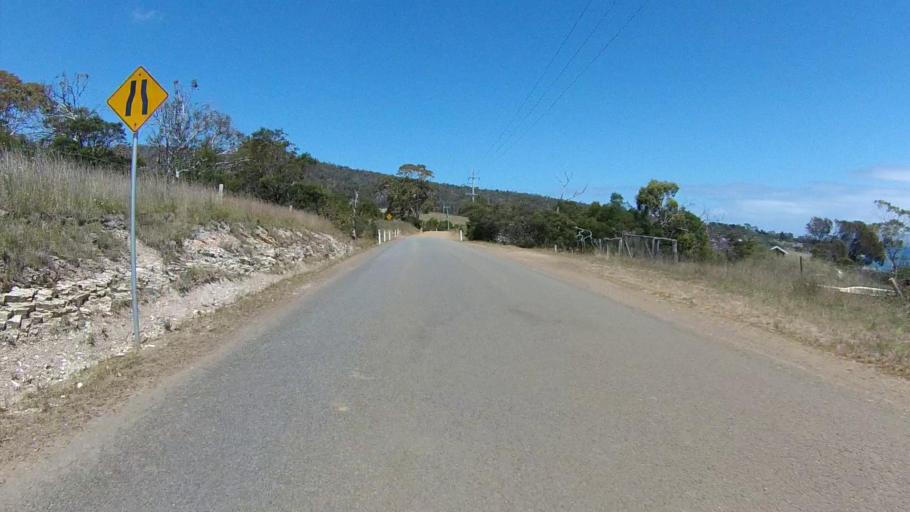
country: AU
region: Tasmania
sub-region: Clarence
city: Lauderdale
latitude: -42.9290
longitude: 147.4657
